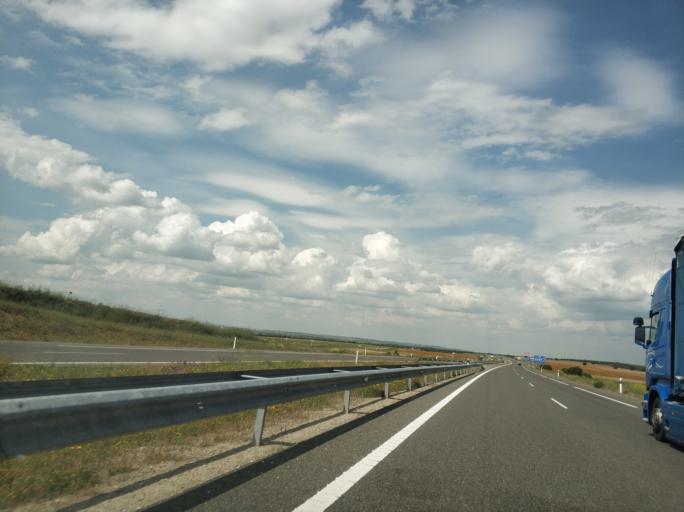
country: ES
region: Castille and Leon
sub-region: Provincia de Salamanca
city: Montejo
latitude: 40.6566
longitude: -5.6262
